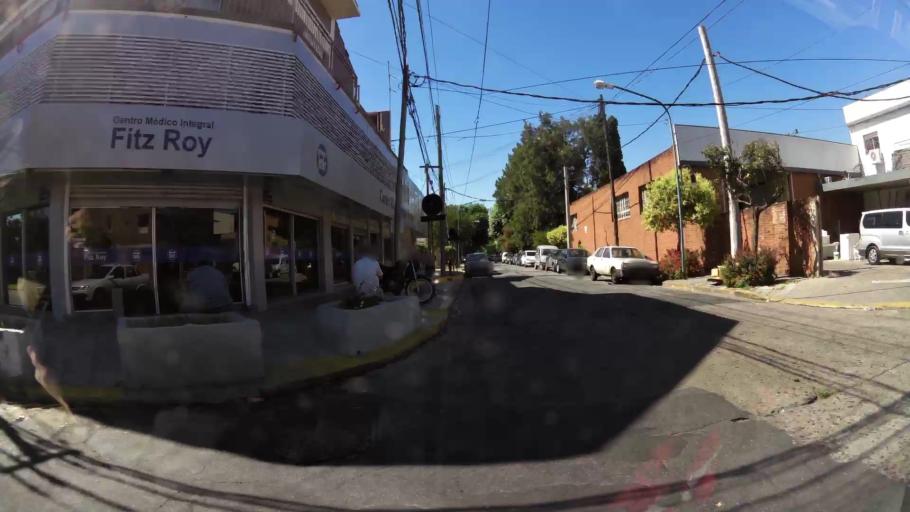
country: AR
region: Buenos Aires
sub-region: Partido de Vicente Lopez
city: Olivos
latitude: -34.5168
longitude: -58.5211
